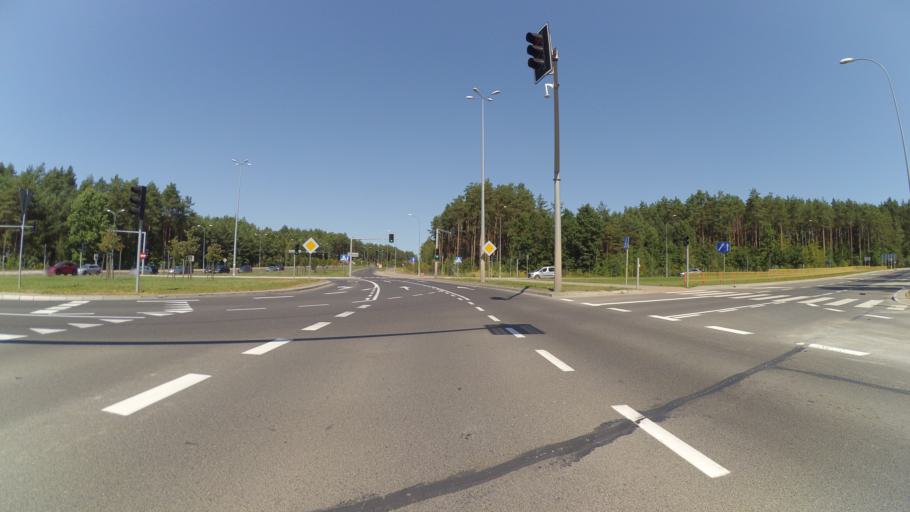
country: PL
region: Podlasie
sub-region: Bialystok
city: Bialystok
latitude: 53.1289
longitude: 23.2237
